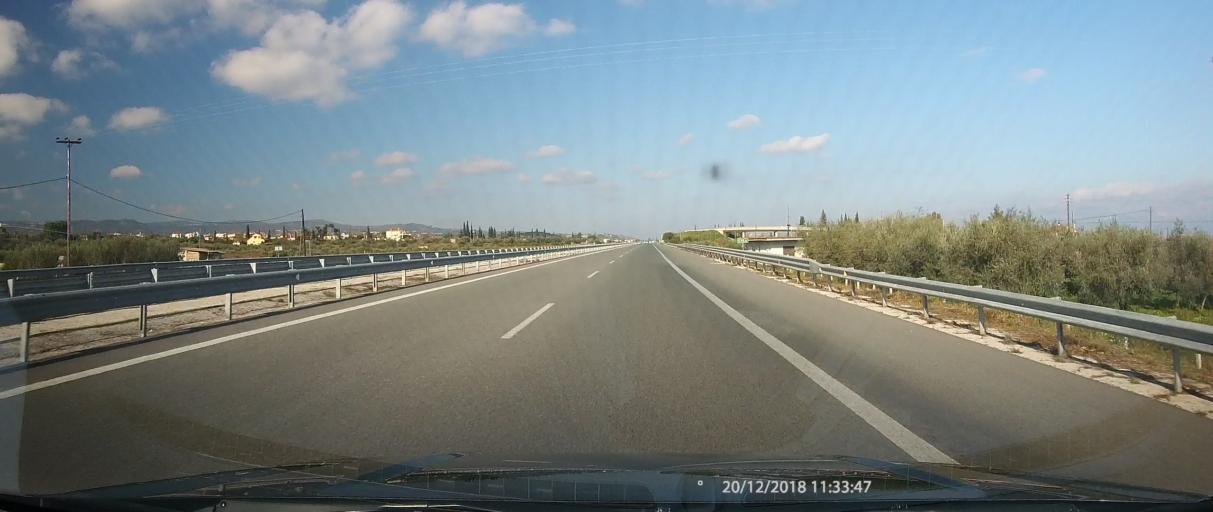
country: GR
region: Peloponnese
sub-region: Nomos Korinthias
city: Velo
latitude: 37.9494
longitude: 22.7564
